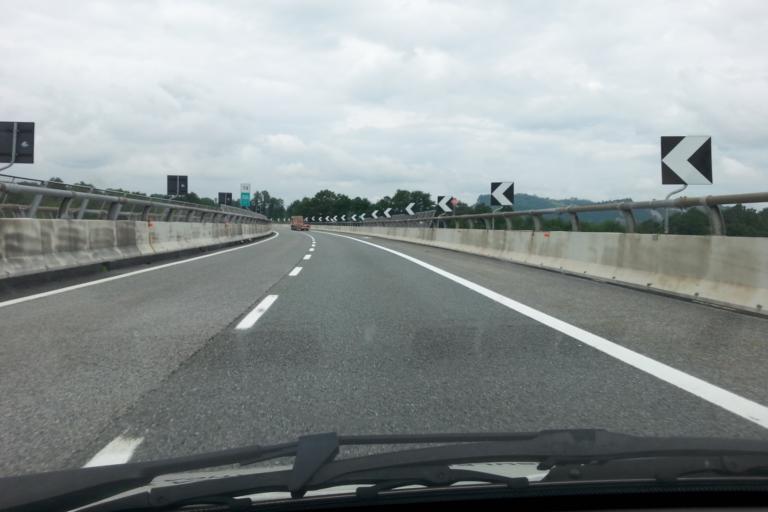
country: IT
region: Piedmont
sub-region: Provincia di Cuneo
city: Lesegno
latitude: 44.4109
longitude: 7.9644
